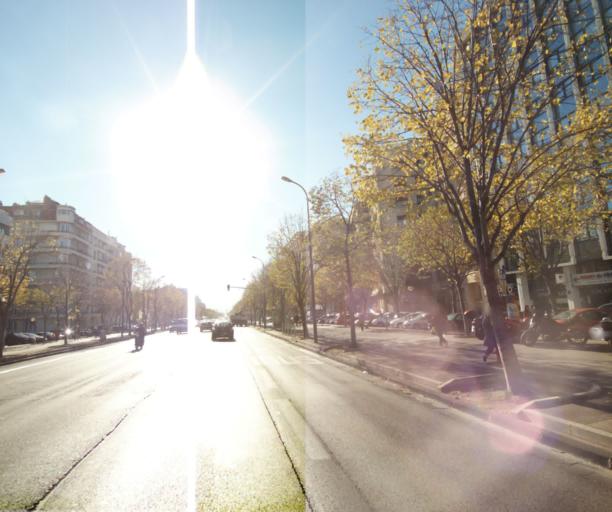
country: FR
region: Provence-Alpes-Cote d'Azur
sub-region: Departement des Bouches-du-Rhone
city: Marseille 08
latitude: 43.2780
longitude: 5.3881
